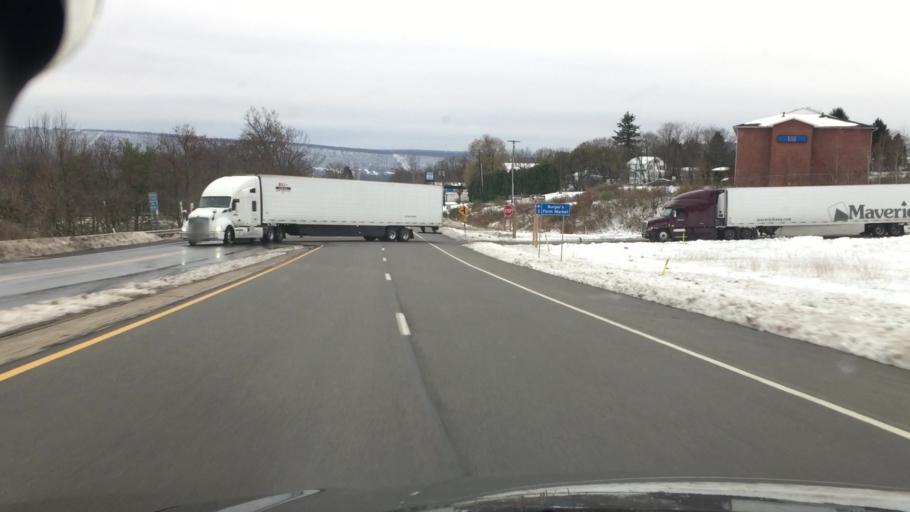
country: US
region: Pennsylvania
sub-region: Luzerne County
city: Conyngham
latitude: 41.0251
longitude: -76.0790
